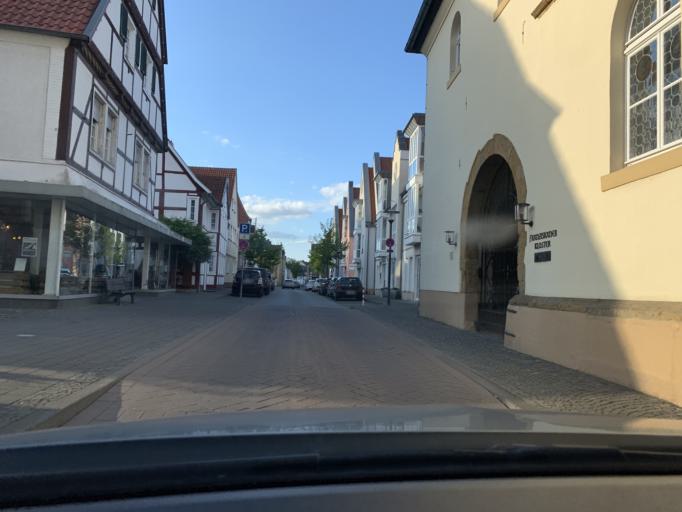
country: DE
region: North Rhine-Westphalia
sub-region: Regierungsbezirk Detmold
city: Rheda-Wiedenbruck
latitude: 51.8360
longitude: 8.3139
